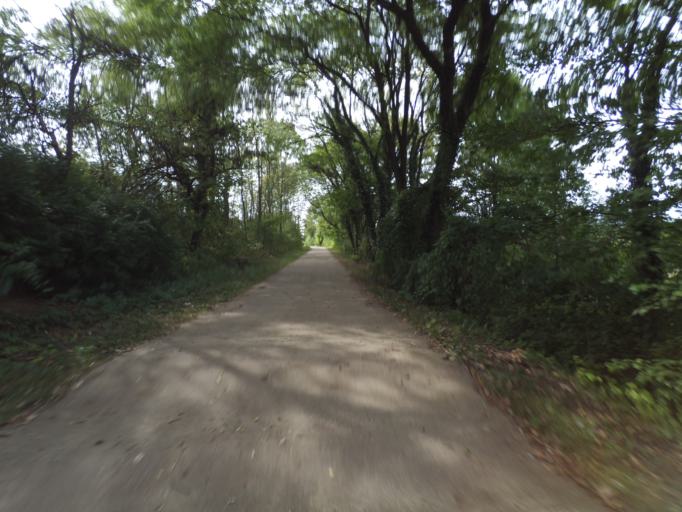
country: LU
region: Grevenmacher
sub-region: Canton de Remich
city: Mondorf-les-Bains
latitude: 49.5195
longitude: 6.3100
